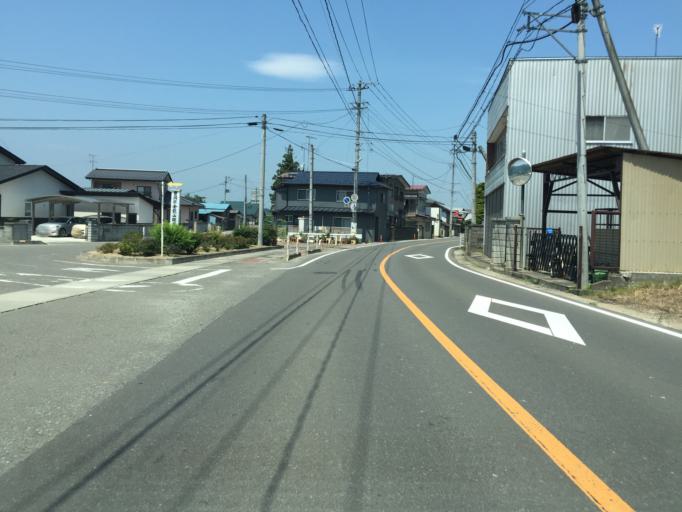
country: JP
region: Miyagi
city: Marumori
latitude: 37.8979
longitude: 140.7994
